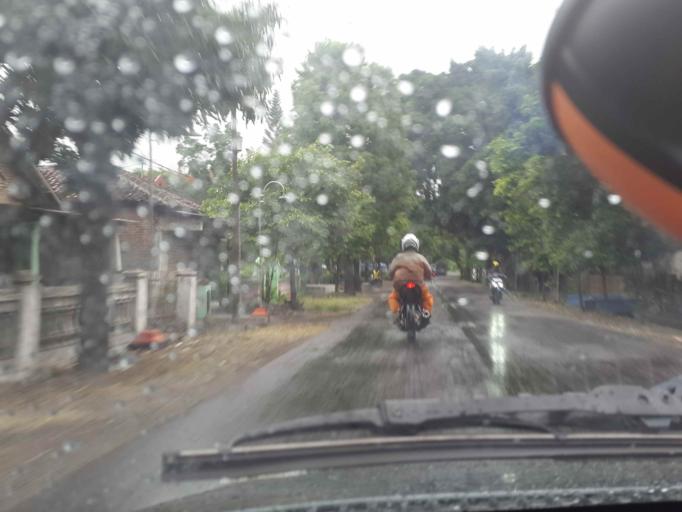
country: ID
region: Central Java
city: Sragen
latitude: -7.4363
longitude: 111.0136
